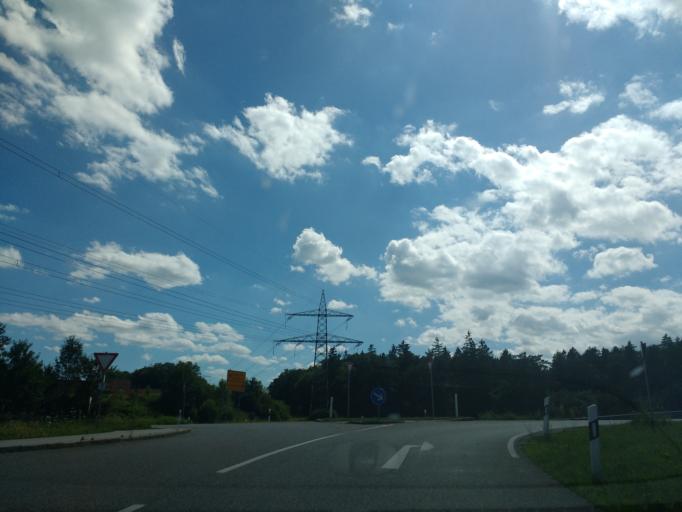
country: DE
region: Bavaria
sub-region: Upper Bavaria
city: Mehring
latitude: 48.2033
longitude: 12.7615
